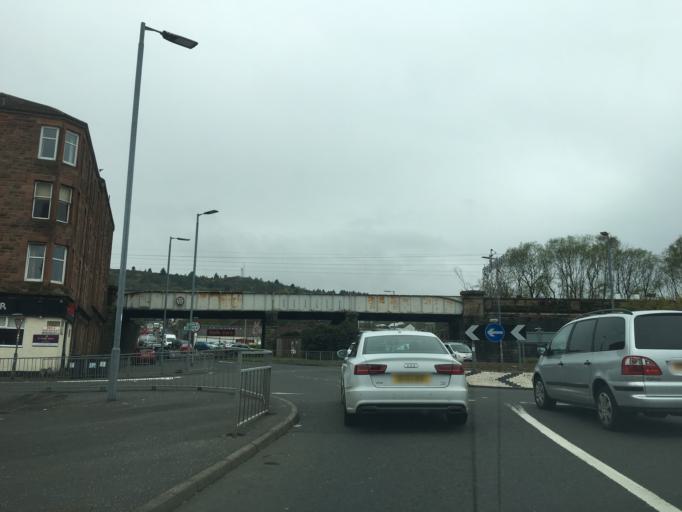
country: GB
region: Scotland
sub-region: Inverclyde
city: Greenock
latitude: 55.9443
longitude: -4.7486
